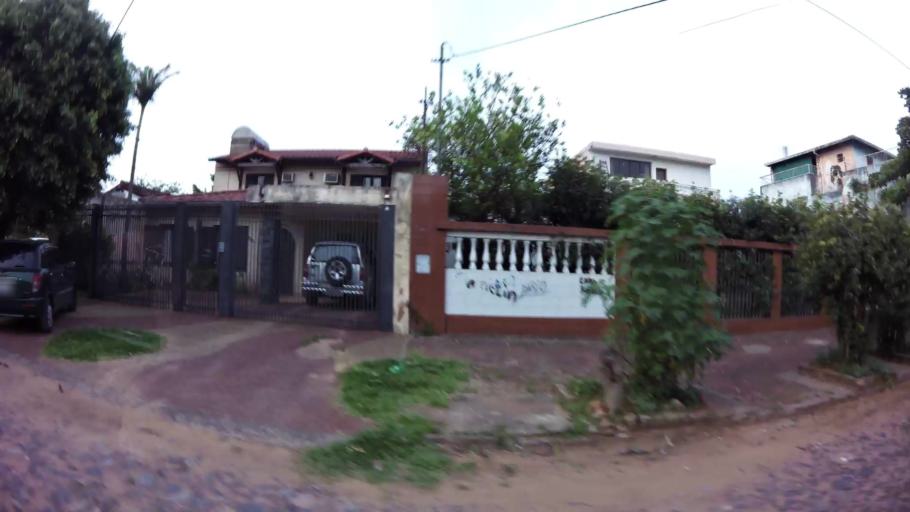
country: PY
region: Asuncion
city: Asuncion
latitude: -25.2999
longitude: -57.6103
